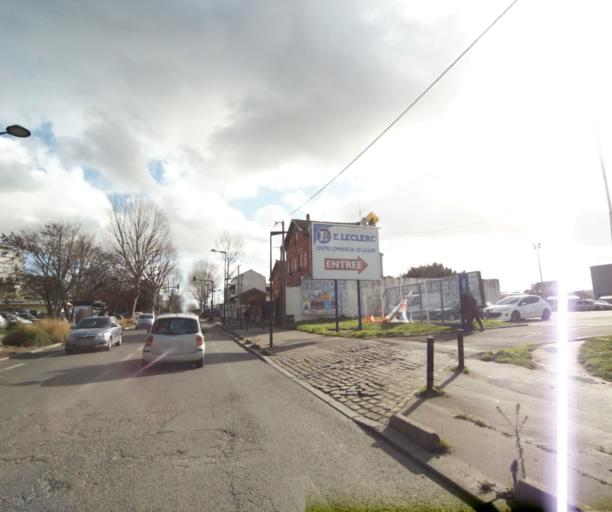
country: FR
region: Ile-de-France
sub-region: Departement de Seine-Saint-Denis
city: Villetaneuse
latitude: 48.9546
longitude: 2.3344
